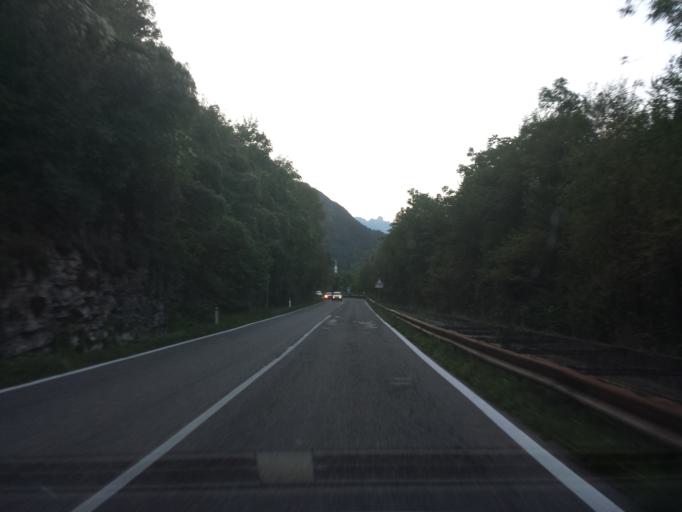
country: IT
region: Veneto
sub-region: Provincia di Vicenza
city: San Quirico
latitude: 45.6689
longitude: 11.2858
